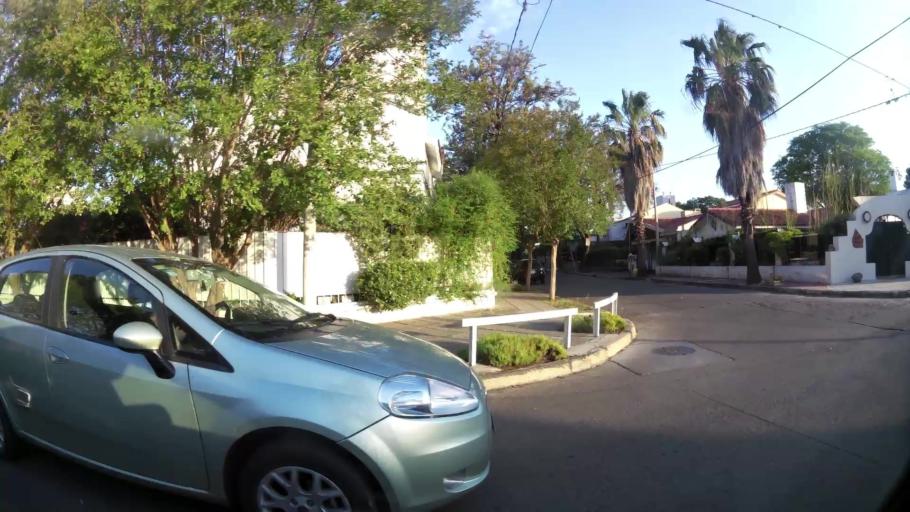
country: AR
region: Cordoba
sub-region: Departamento de Capital
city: Cordoba
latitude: -31.3773
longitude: -64.2382
